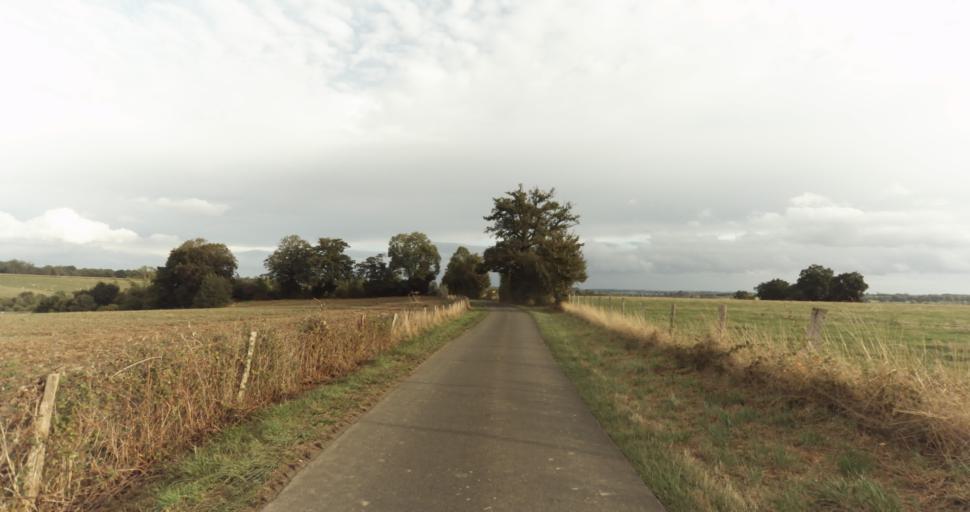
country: FR
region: Lower Normandy
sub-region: Departement de l'Orne
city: Sees
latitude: 48.6883
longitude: 0.2317
